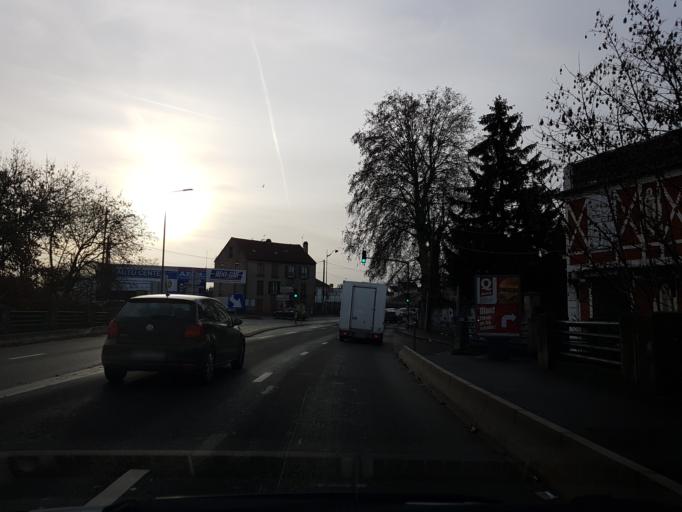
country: FR
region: Ile-de-France
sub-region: Departement du Val-de-Marne
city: Villeneuve-Saint-Georges
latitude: 48.7253
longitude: 2.4448
